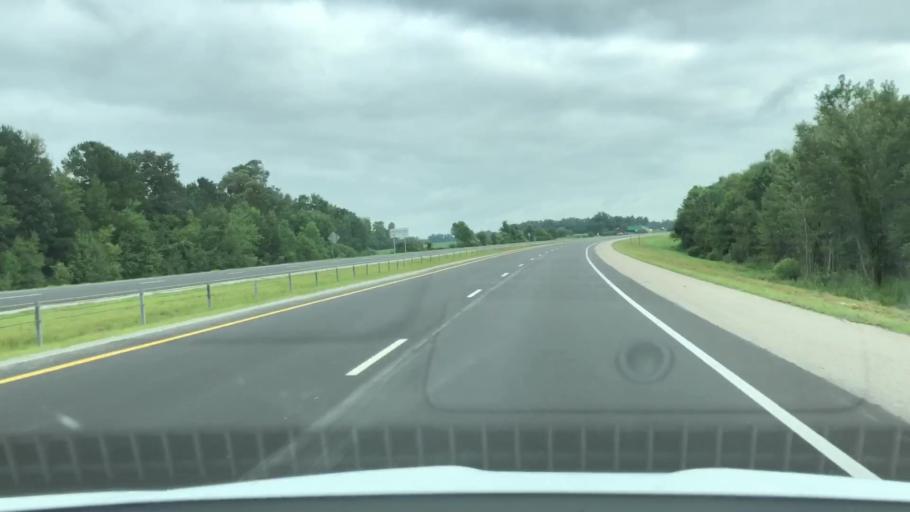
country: US
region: North Carolina
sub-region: Wayne County
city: Fremont
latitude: 35.5843
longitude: -77.9894
